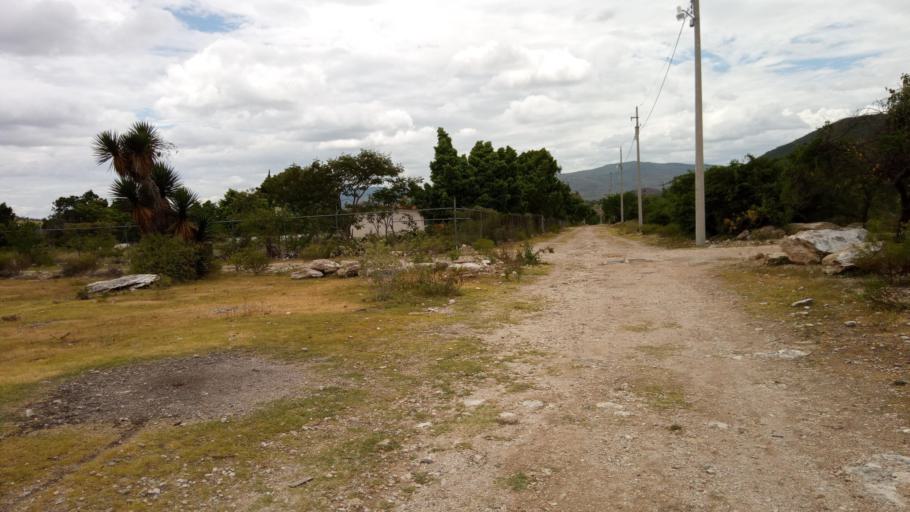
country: MX
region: Puebla
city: Totoltepec de Guerrero
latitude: 18.2954
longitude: -97.7727
